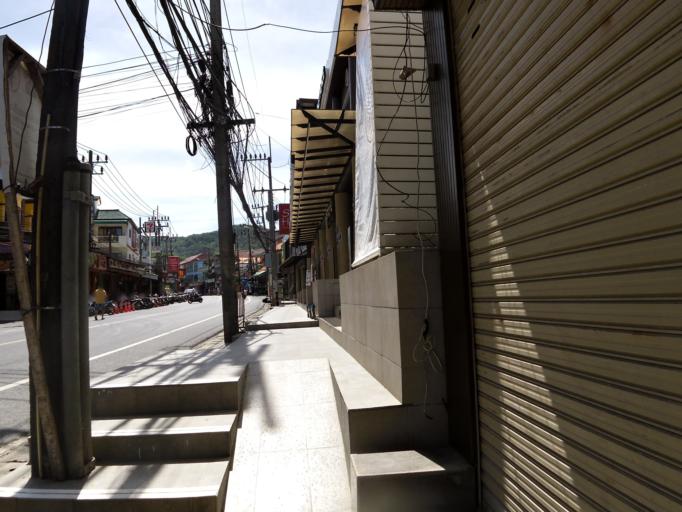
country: TH
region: Phuket
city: Ban Karon
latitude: 7.8484
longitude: 98.2947
